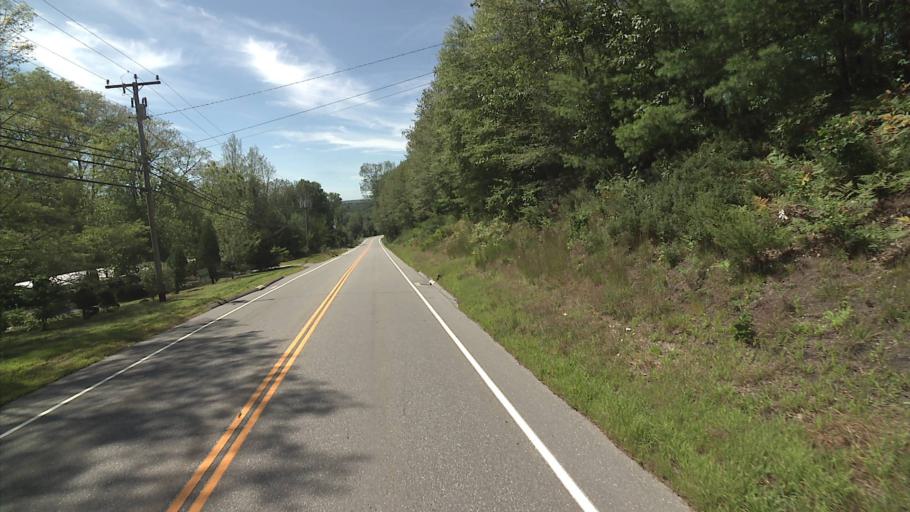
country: US
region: Connecticut
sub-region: Windham County
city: Killingly Center
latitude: 41.8411
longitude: -71.8500
